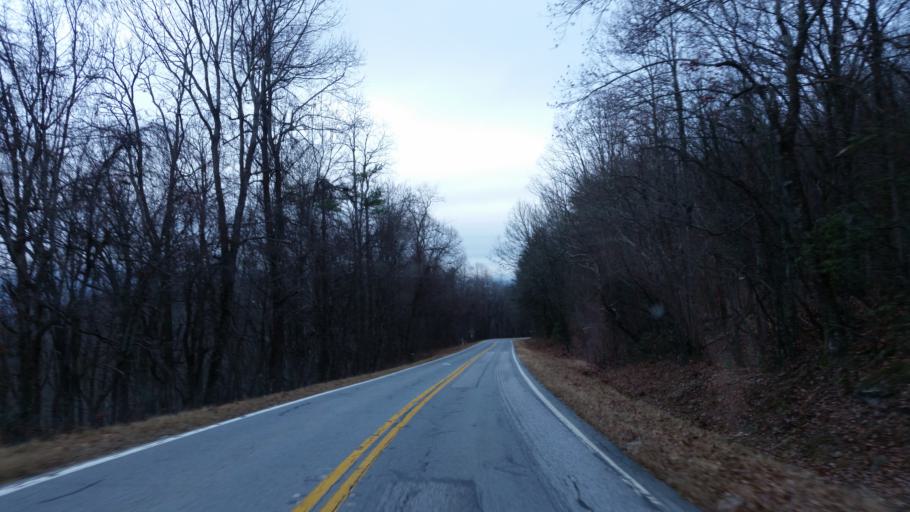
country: US
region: Georgia
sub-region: Pickens County
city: Jasper
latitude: 34.5457
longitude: -84.3295
